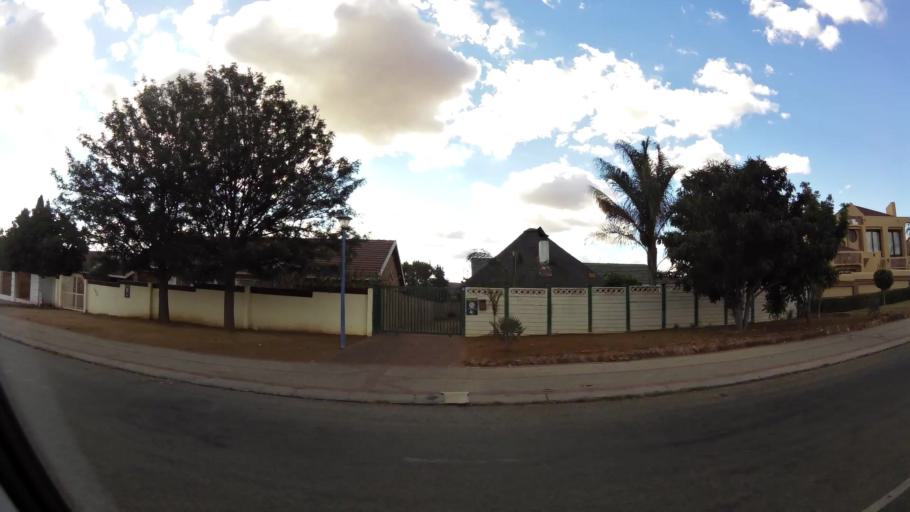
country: ZA
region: Limpopo
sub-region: Capricorn District Municipality
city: Polokwane
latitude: -23.9169
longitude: 29.4992
